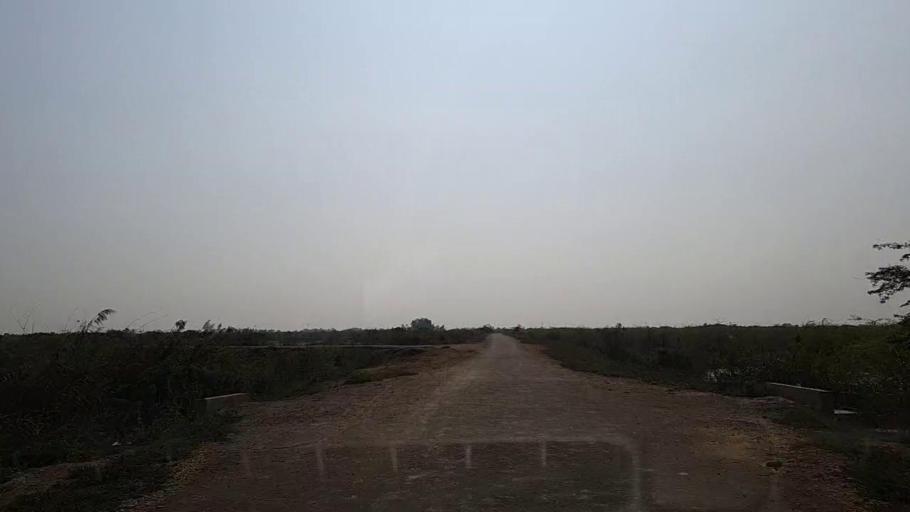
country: PK
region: Sindh
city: Mirpur Sakro
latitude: 24.6553
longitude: 67.6914
